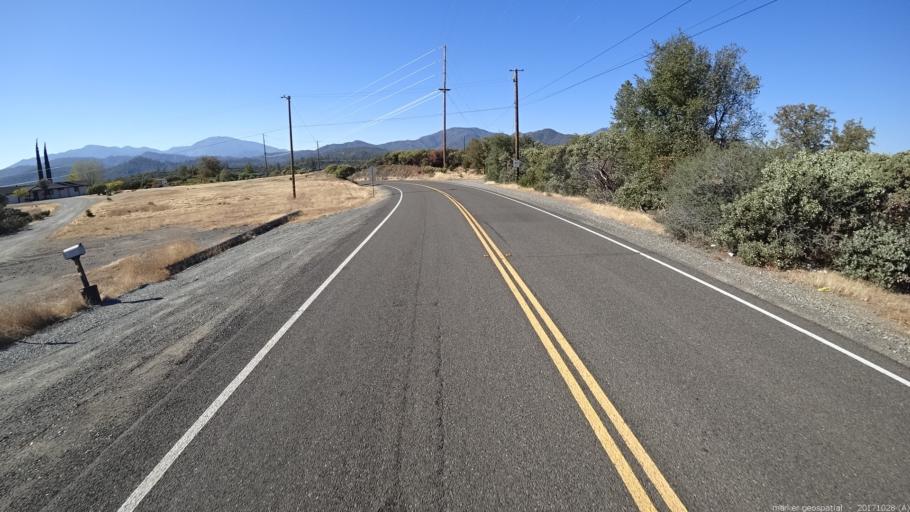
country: US
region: California
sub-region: Shasta County
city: Redding
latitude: 40.6155
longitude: -122.4384
